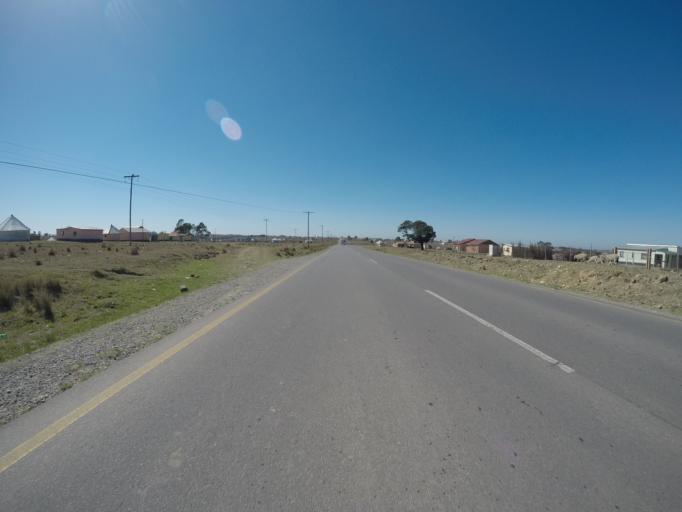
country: ZA
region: Eastern Cape
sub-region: OR Tambo District Municipality
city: Mthatha
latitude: -31.8972
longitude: 28.7869
